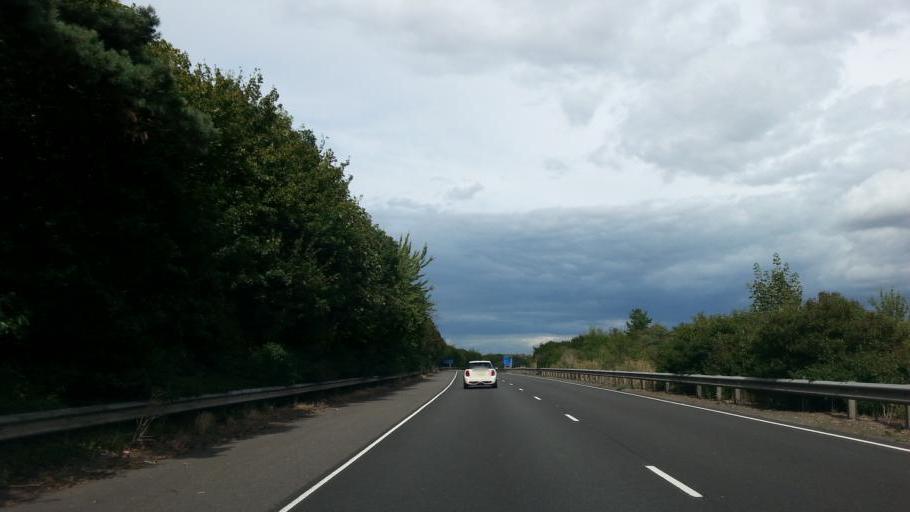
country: GB
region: England
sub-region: Cambridgeshire
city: Duxford
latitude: 52.0661
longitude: 0.1856
